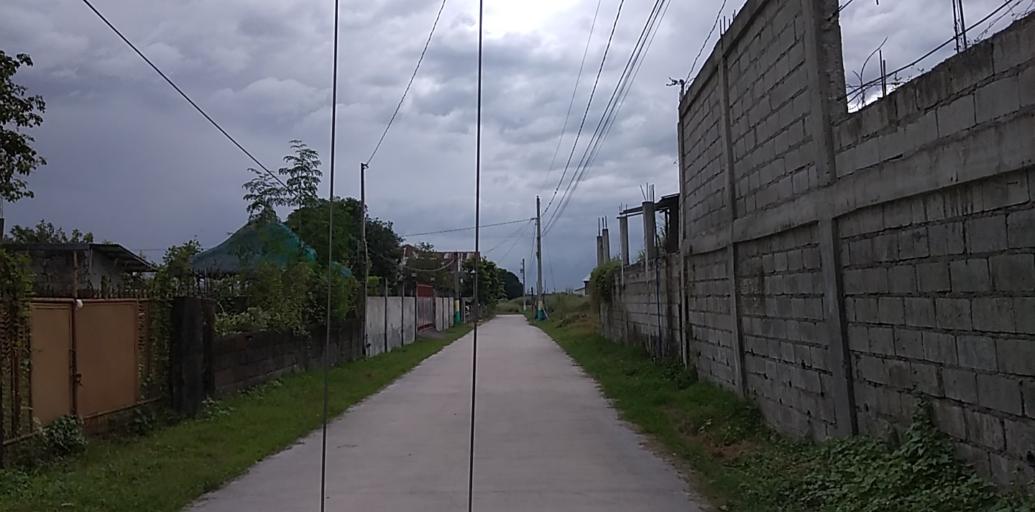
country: PH
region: Central Luzon
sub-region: Province of Pampanga
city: Porac
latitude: 15.0618
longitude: 120.5421
